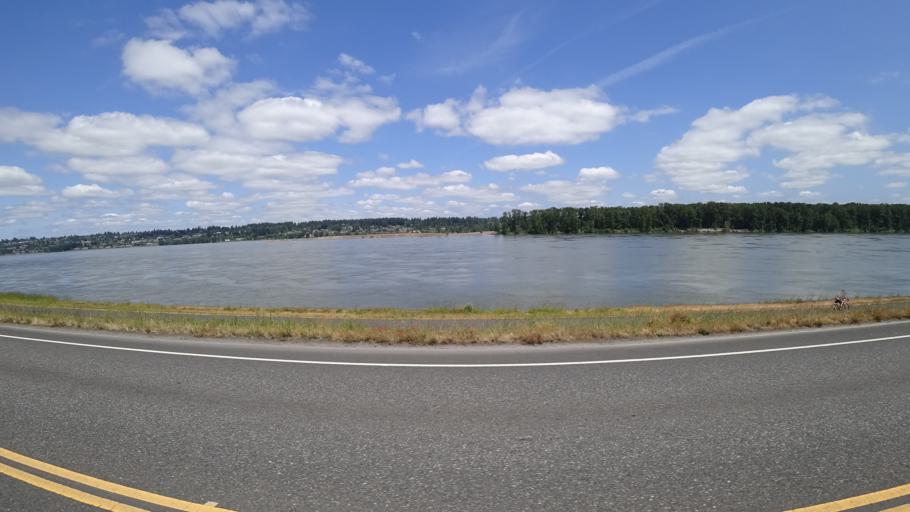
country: US
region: Washington
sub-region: Clark County
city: Orchards
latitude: 45.5896
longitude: -122.5762
